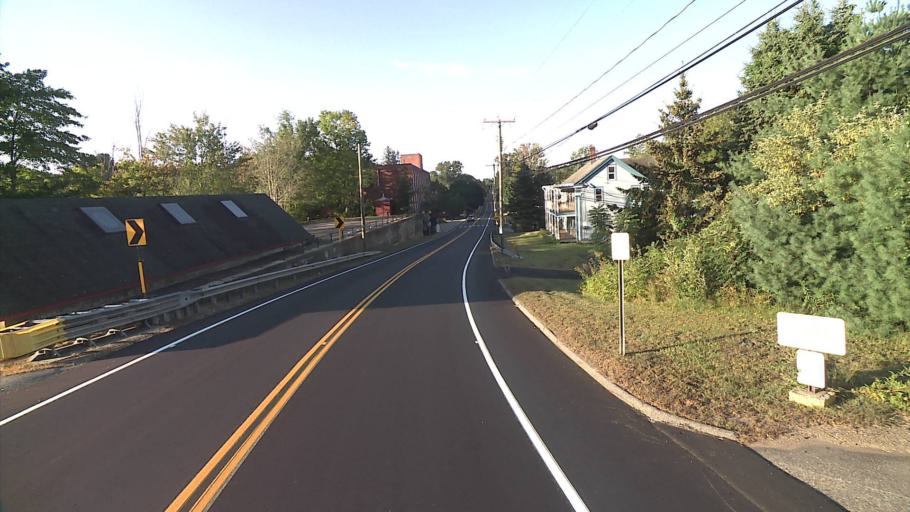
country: US
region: Connecticut
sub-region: Tolland County
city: Storrs
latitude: 41.8576
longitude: -72.2994
